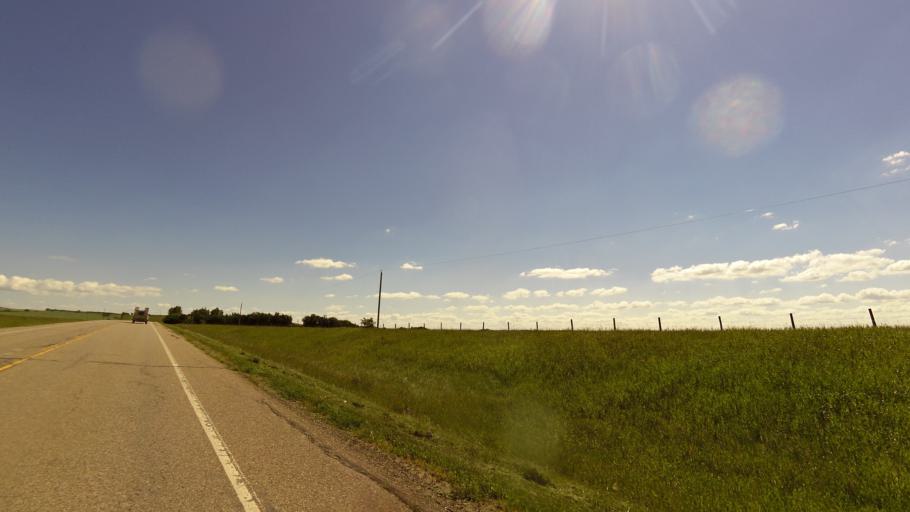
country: CA
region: Saskatchewan
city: Lloydminster
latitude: 52.8417
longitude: -110.0253
